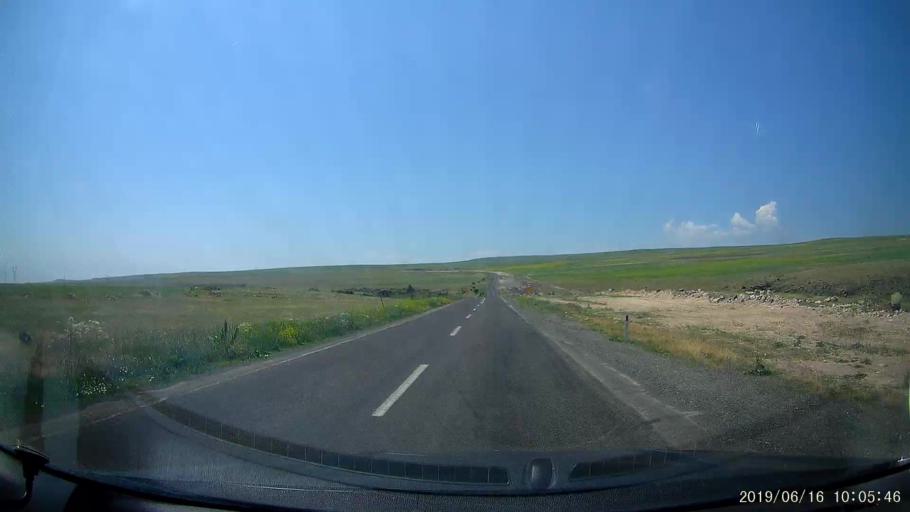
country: TR
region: Kars
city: Digor
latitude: 40.2657
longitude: 43.5395
